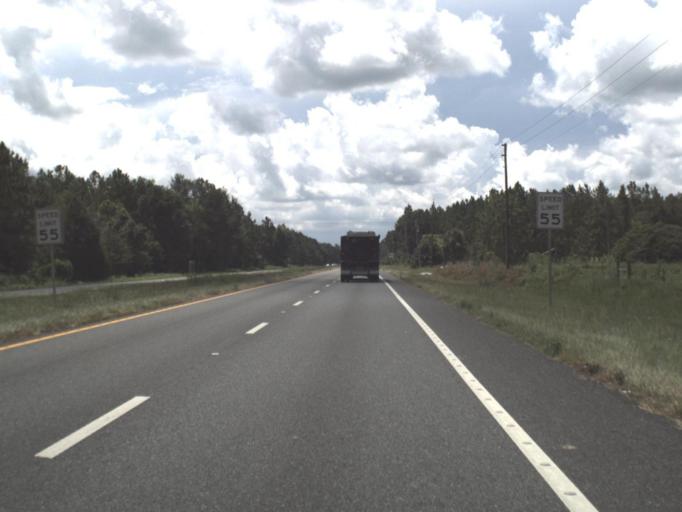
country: US
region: Florida
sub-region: Taylor County
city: Perry
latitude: 30.1438
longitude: -83.6097
